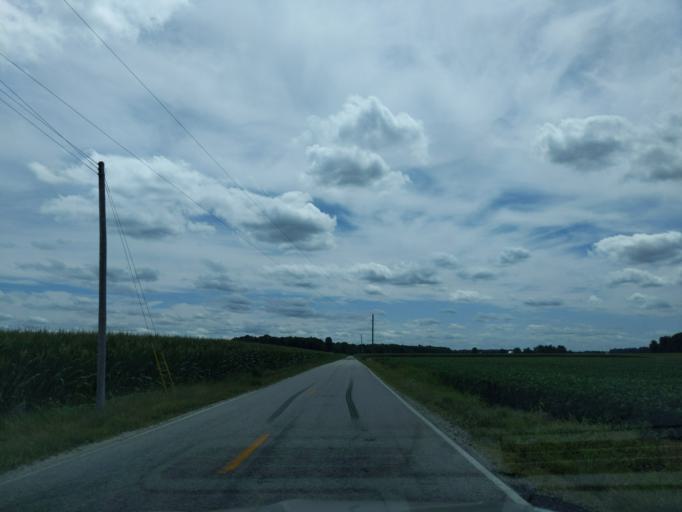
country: US
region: Indiana
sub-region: Ripley County
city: Batesville
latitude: 39.2279
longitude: -85.2680
